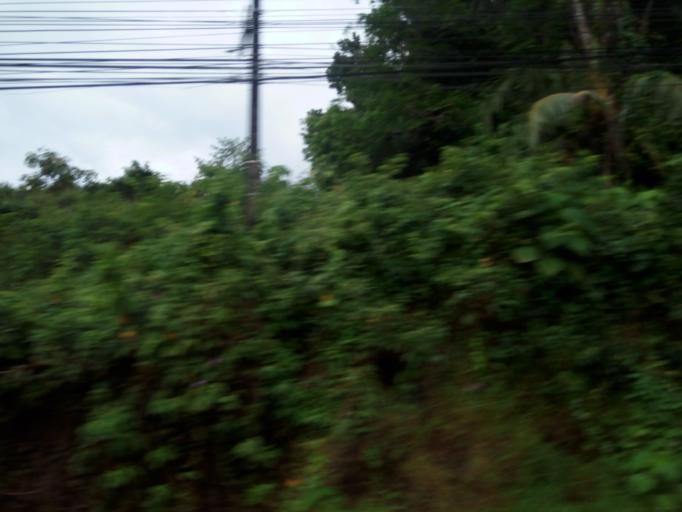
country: TH
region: Phuket
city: Thalang
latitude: 8.0905
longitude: 98.3628
